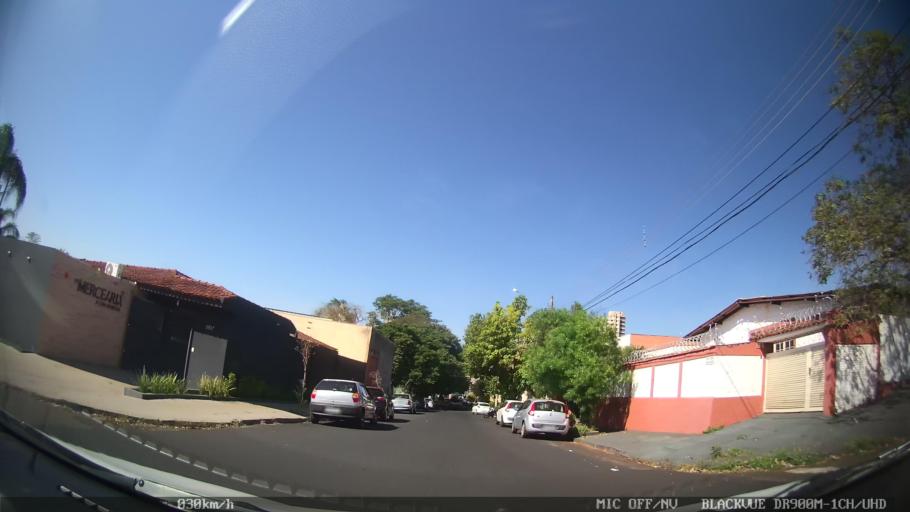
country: BR
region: Sao Paulo
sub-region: Ribeirao Preto
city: Ribeirao Preto
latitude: -21.1970
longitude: -47.8009
